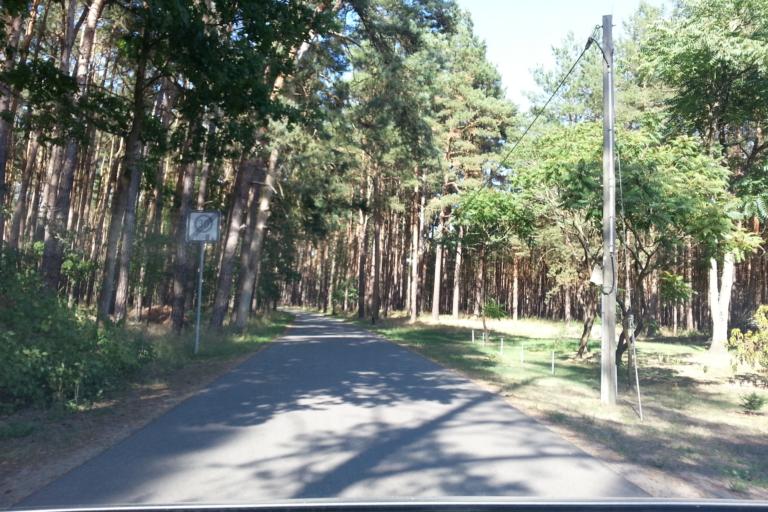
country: DE
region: Mecklenburg-Vorpommern
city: Eggesin
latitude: 53.6875
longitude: 14.0456
